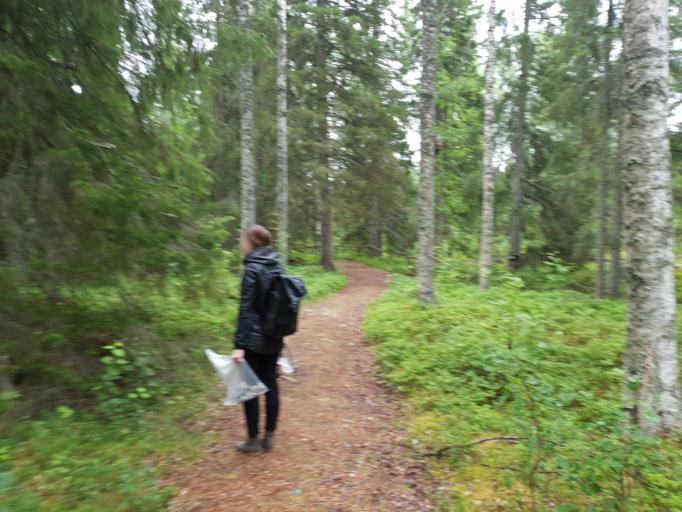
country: SE
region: Vaesterbotten
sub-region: Skelleftea Kommun
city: Viken
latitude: 64.8006
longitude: 20.7378
